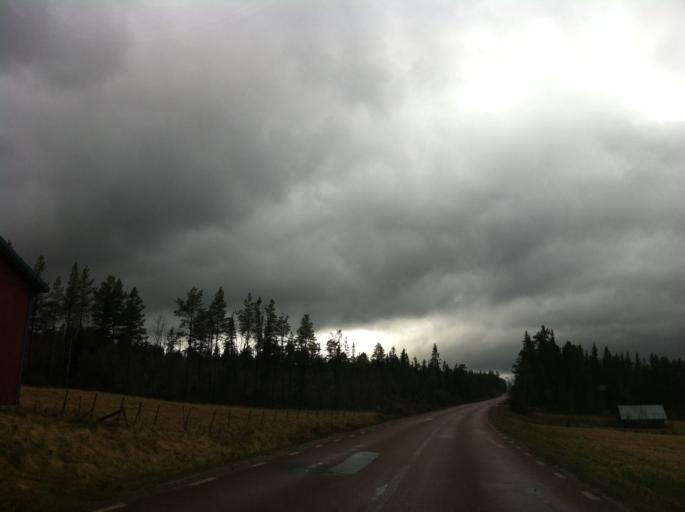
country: NO
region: Hedmark
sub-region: Engerdal
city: Engerdal
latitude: 62.4349
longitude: 12.7136
